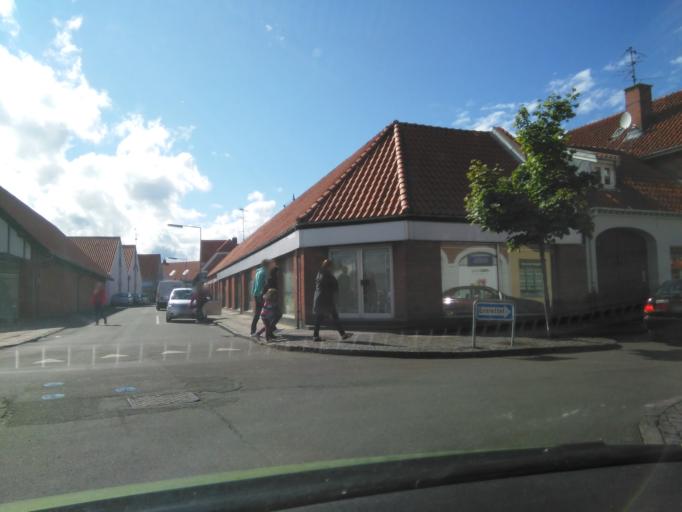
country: DK
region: Capital Region
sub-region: Bornholm Kommune
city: Nexo
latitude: 55.0621
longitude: 15.1327
